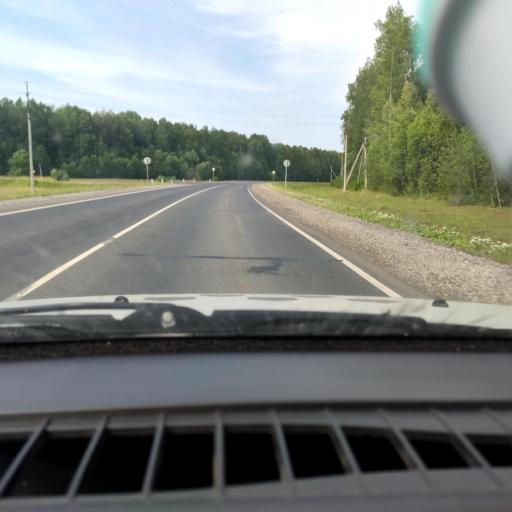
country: RU
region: Perm
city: Siva
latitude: 58.6046
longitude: 53.8680
